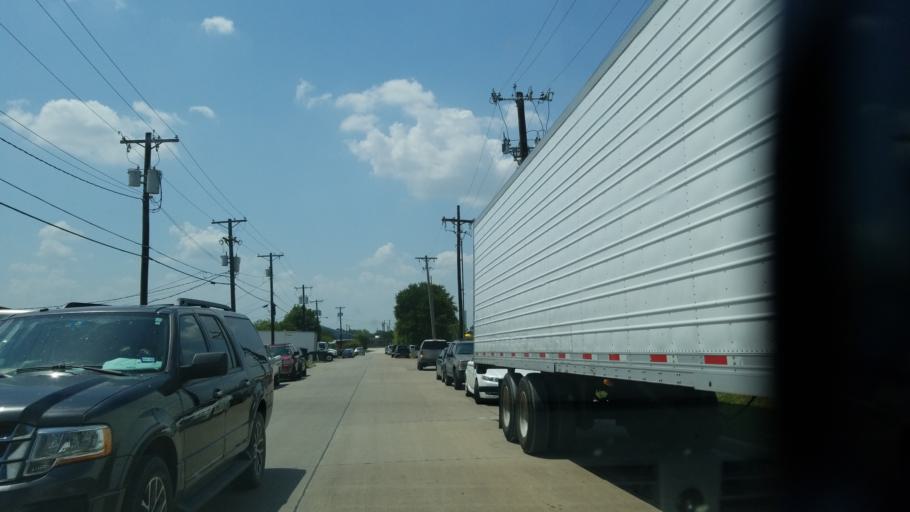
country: US
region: Texas
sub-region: Dallas County
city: Garland
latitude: 32.9214
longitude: -96.6324
